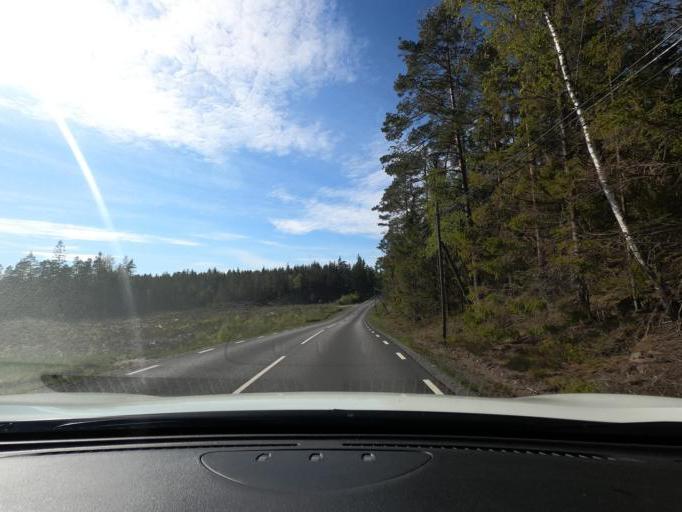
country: SE
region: Vaestra Goetaland
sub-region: Harryda Kommun
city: Landvetter
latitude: 57.6351
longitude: 12.2624
